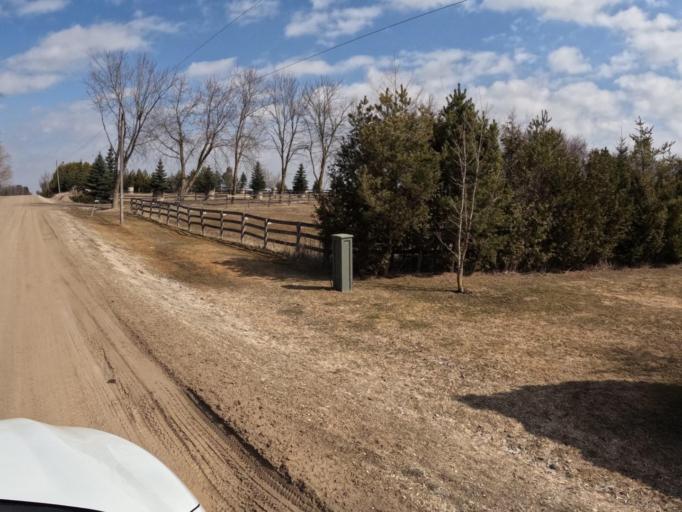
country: CA
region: Ontario
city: Orangeville
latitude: 43.9016
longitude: -80.2510
